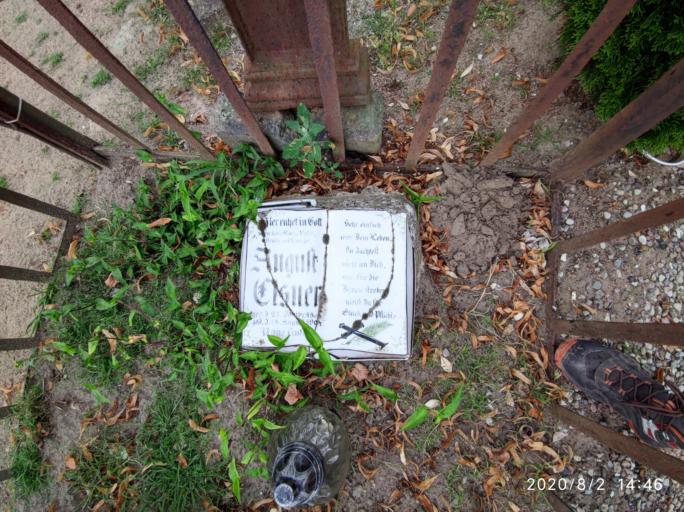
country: PL
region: Lubusz
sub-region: Powiat swiebodzinski
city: Lubrza
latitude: 52.3755
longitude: 15.4603
